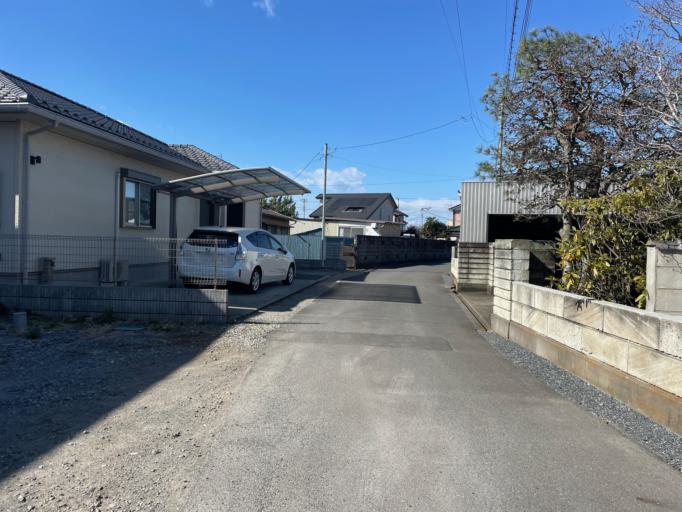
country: JP
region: Saitama
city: Kawagoe
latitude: 35.9486
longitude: 139.4567
